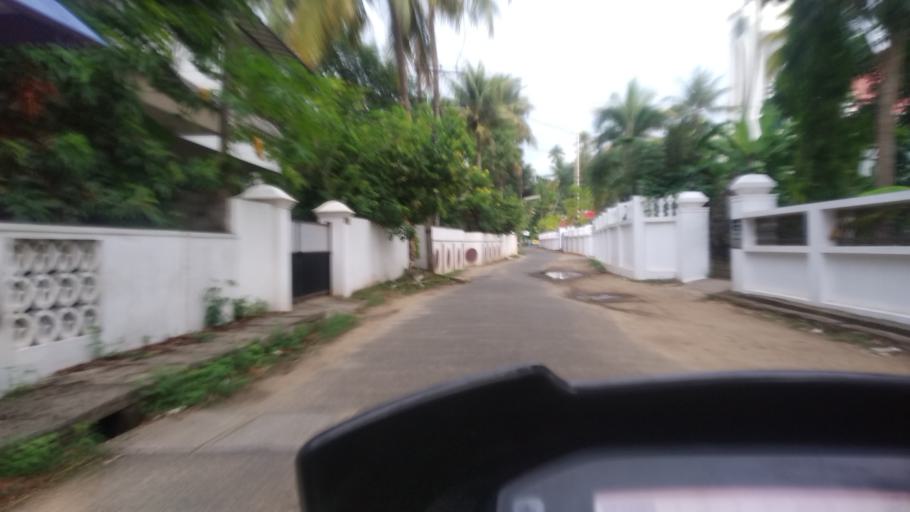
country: IN
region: Kerala
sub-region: Ernakulam
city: Elur
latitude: 10.0633
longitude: 76.2151
